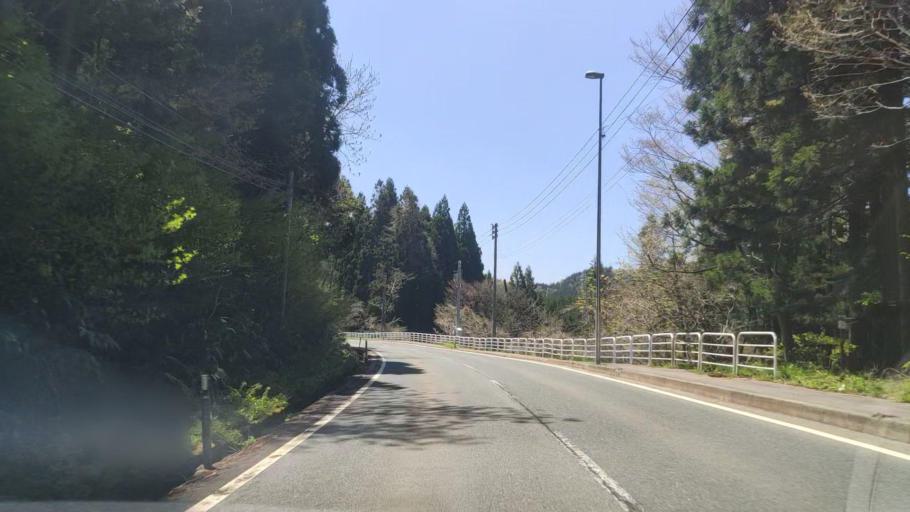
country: JP
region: Yamagata
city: Shinjo
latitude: 38.8961
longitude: 140.3261
